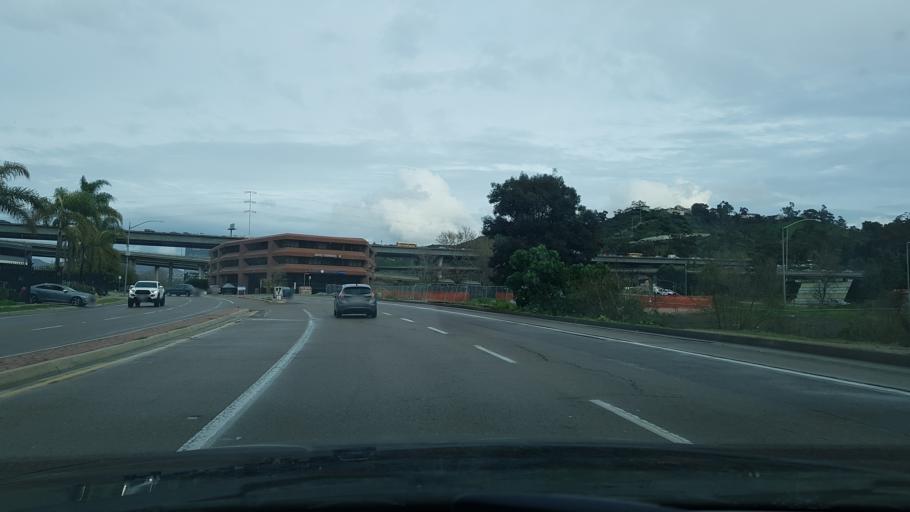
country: US
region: California
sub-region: San Diego County
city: San Diego
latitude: 32.7720
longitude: -117.1368
